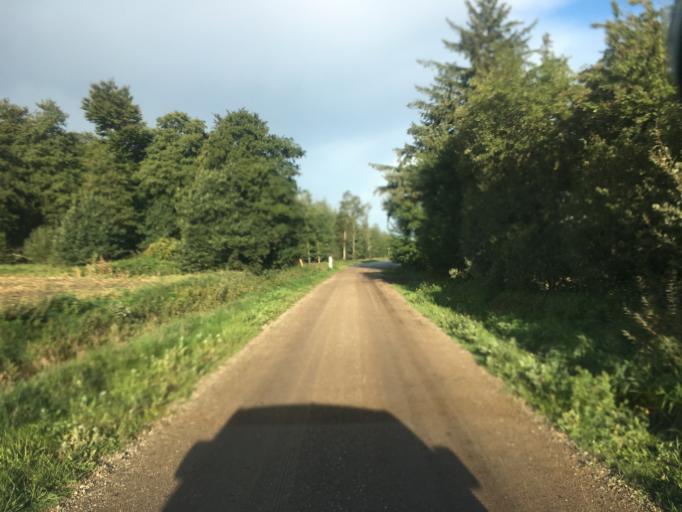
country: DE
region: Schleswig-Holstein
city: Ellhoft
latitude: 54.9646
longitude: 8.9786
